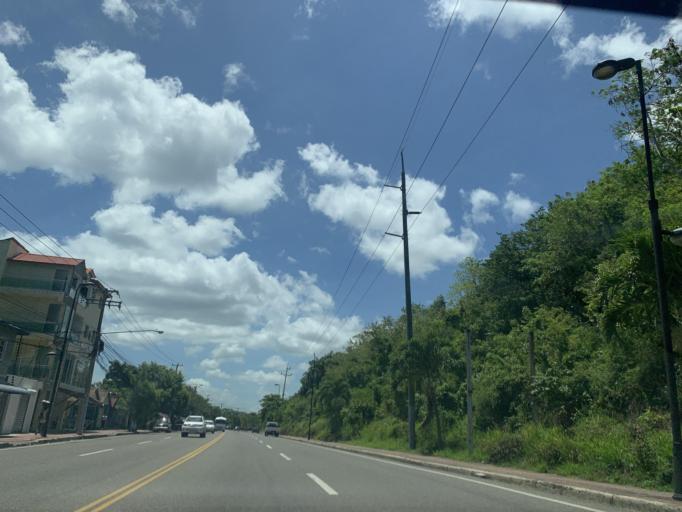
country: DO
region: Puerto Plata
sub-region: Puerto Plata
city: Puerto Plata
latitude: 19.7735
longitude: -70.6570
